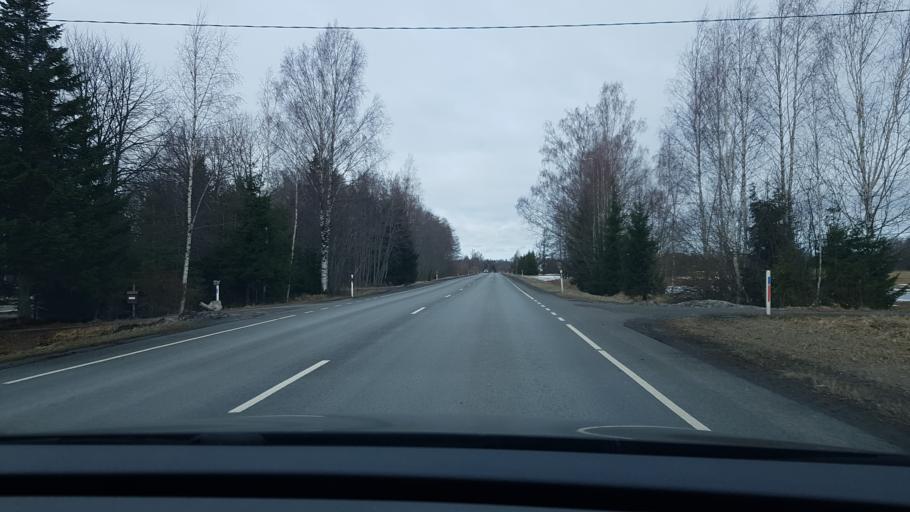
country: EE
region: Paernumaa
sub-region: Paikuse vald
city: Paikuse
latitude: 58.2278
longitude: 24.7014
